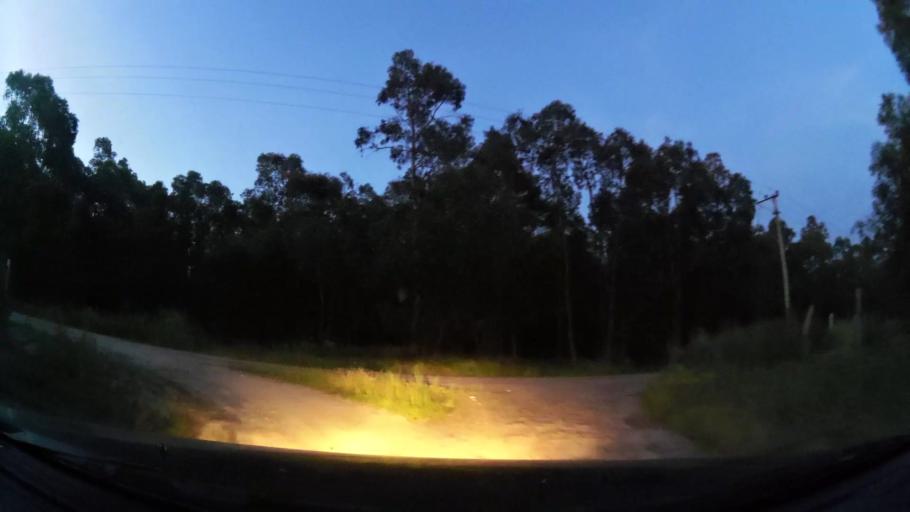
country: UY
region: Canelones
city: Atlantida
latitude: -34.7621
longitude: -55.7555
